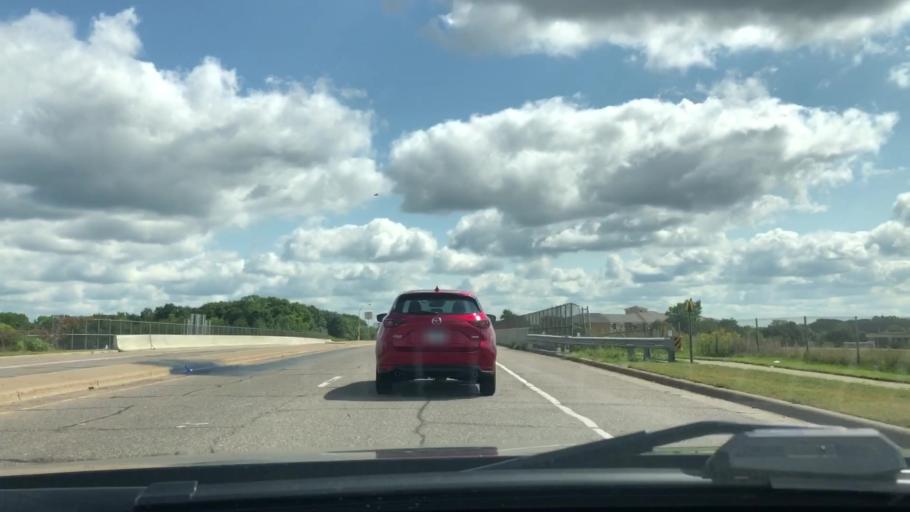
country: US
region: Minnesota
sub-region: Dakota County
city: Mendota Heights
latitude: 44.8479
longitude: -93.1546
